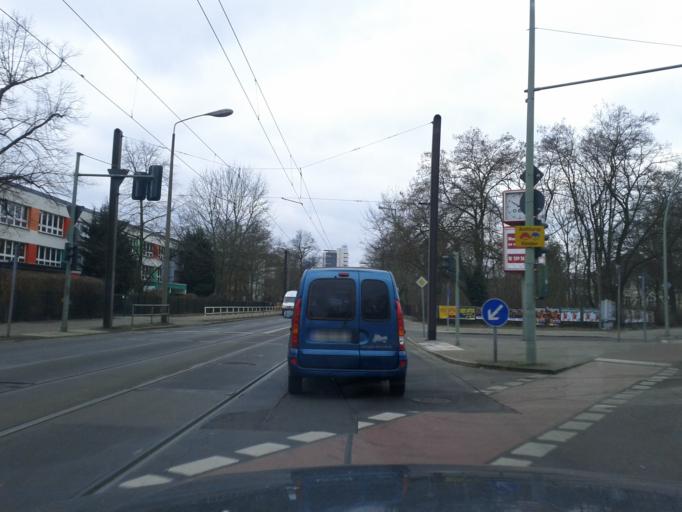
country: DE
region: Berlin
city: Oberschoneweide
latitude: 52.4577
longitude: 13.5426
